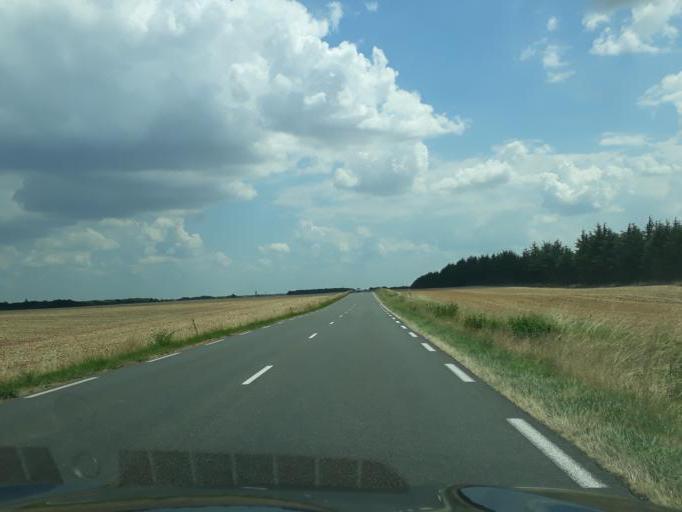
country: FR
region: Centre
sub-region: Departement du Cher
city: Avord
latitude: 47.0382
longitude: 2.5956
